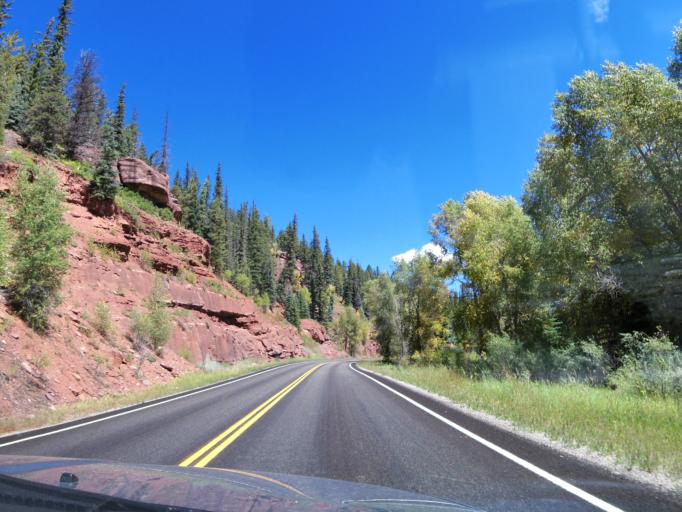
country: US
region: Colorado
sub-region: Montezuma County
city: Mancos
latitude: 37.6032
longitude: -108.1088
